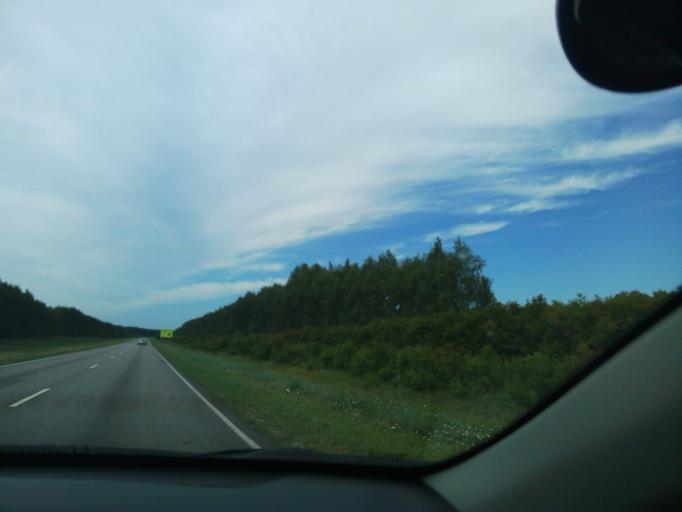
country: RU
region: Tambov
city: Zavoronezhskoye
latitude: 52.6116
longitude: 40.7739
